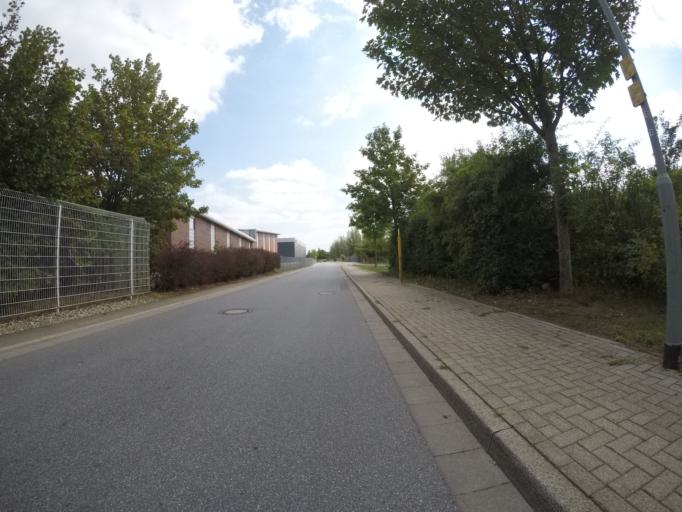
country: DE
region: North Rhine-Westphalia
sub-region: Regierungsbezirk Munster
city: Isselburg
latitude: 51.8179
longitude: 6.4471
